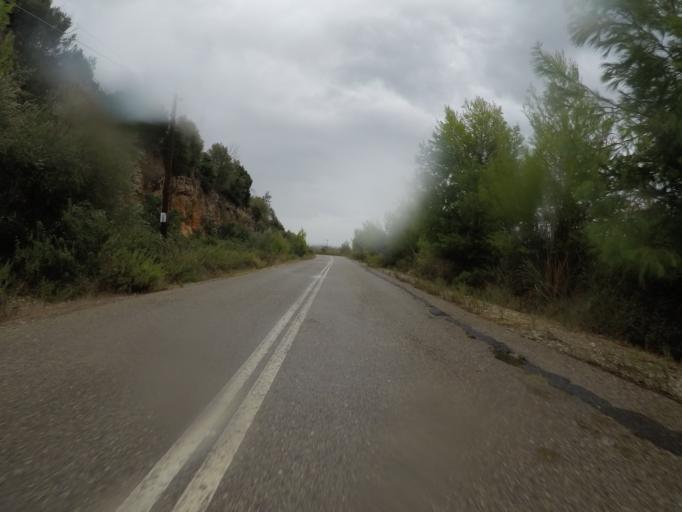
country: GR
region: West Greece
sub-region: Nomos Ileias
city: Zacharo
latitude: 37.5251
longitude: 21.5944
